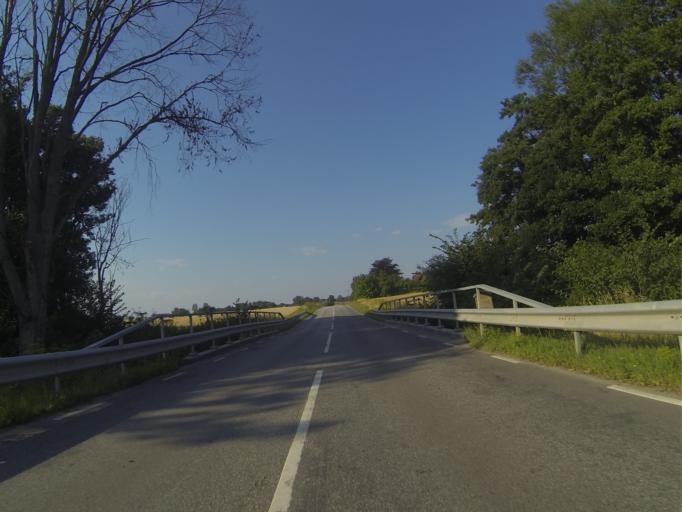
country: SE
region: Skane
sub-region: Lunds Kommun
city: Genarp
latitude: 55.6073
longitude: 13.4043
